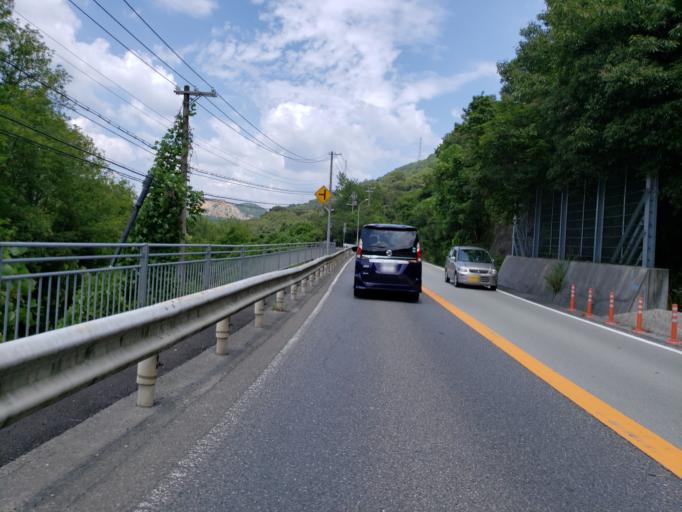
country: JP
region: Hyogo
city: Aioi
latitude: 34.7741
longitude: 134.4311
